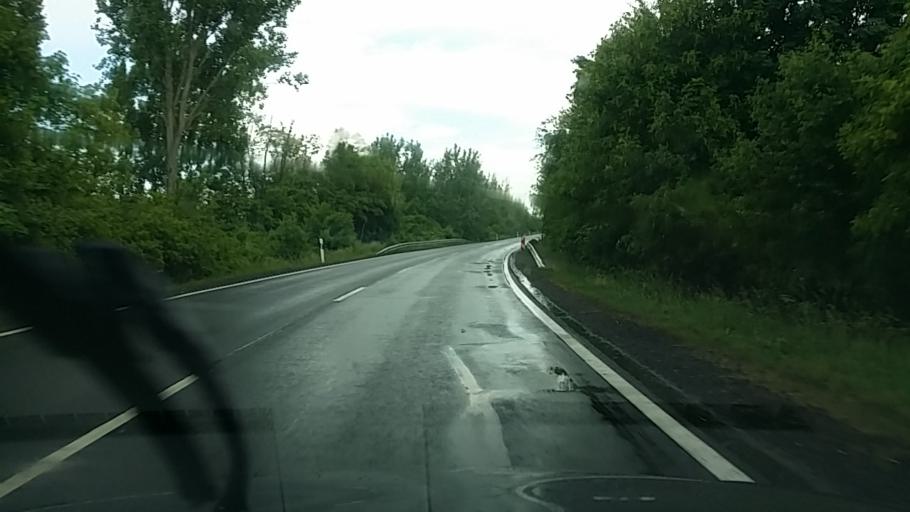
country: HU
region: Nograd
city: Nagyoroszi
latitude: 48.0162
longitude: 19.0754
